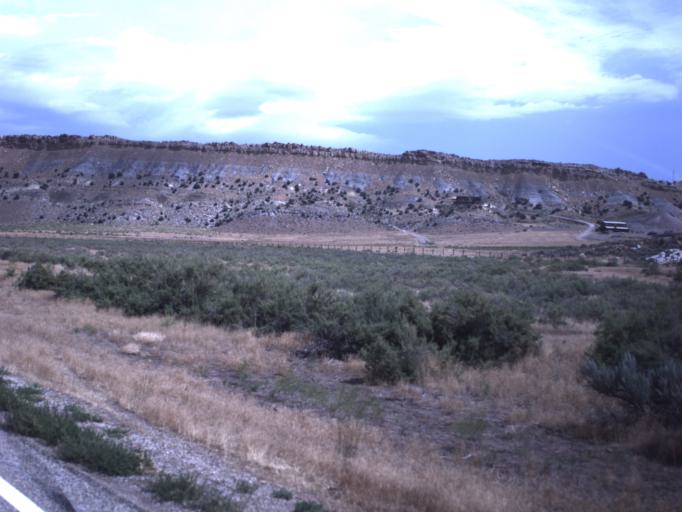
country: US
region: Utah
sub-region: Uintah County
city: Vernal
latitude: 40.5333
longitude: -109.5221
